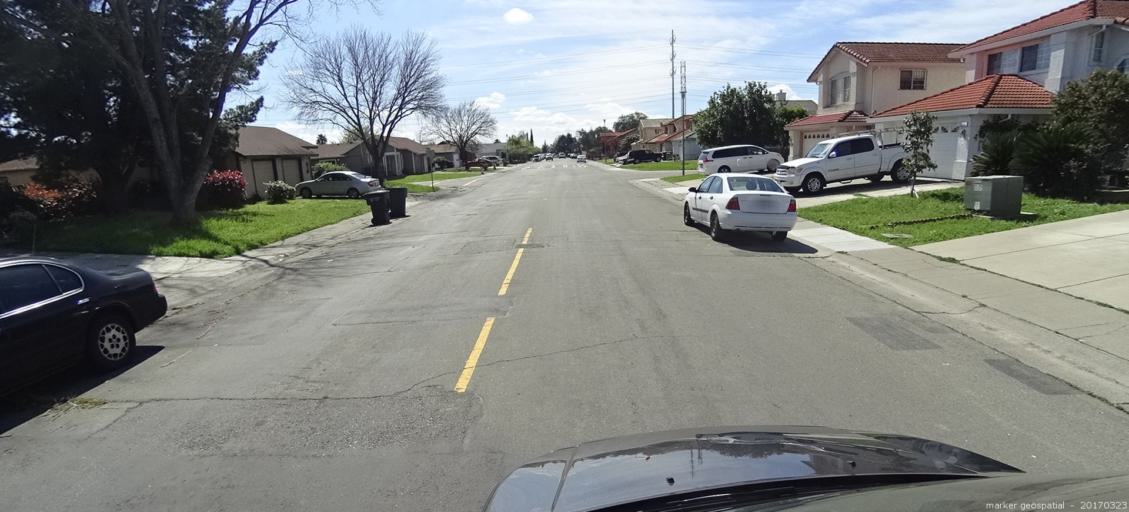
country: US
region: California
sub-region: Sacramento County
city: Florin
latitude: 38.5103
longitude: -121.4189
